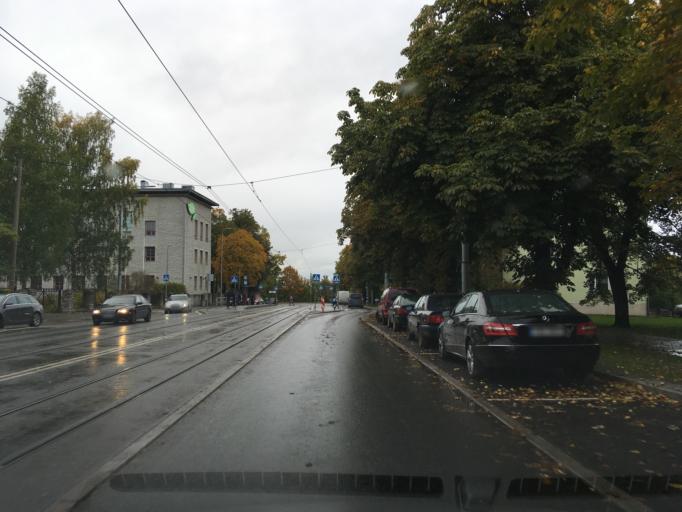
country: EE
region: Harju
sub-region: Tallinna linn
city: Tallinn
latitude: 59.4296
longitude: 24.7876
